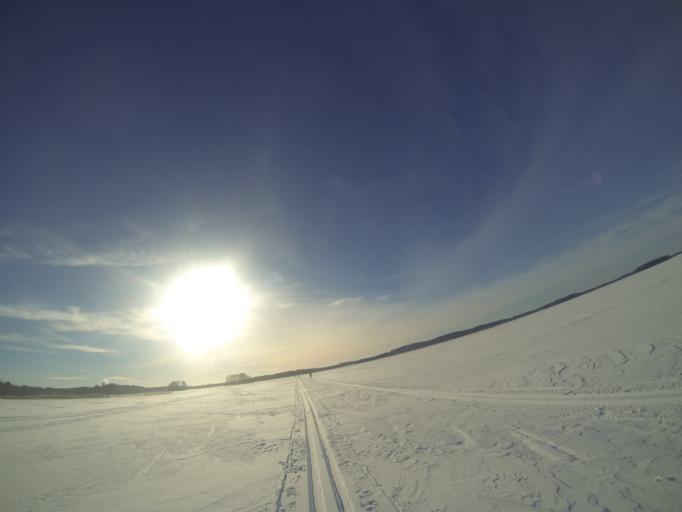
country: FI
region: Southern Savonia
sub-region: Savonlinna
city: Savonlinna
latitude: 61.8916
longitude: 28.9072
